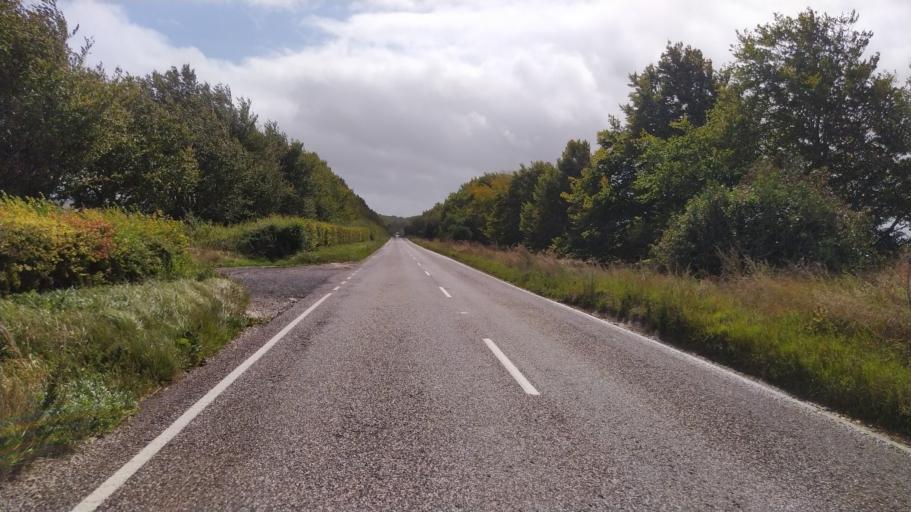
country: GB
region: England
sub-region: Wiltshire
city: Bower Chalke
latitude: 50.9434
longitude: -1.9750
